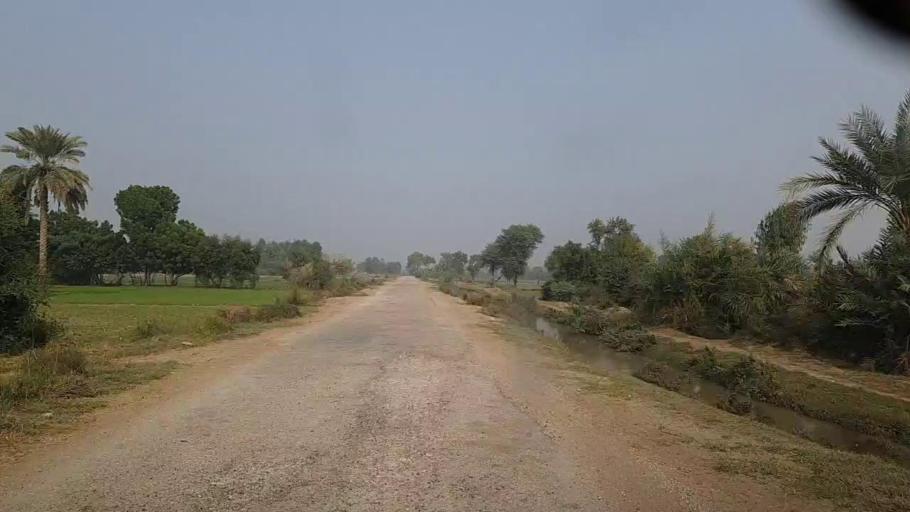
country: PK
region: Sindh
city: Bozdar
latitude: 27.0628
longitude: 68.6357
